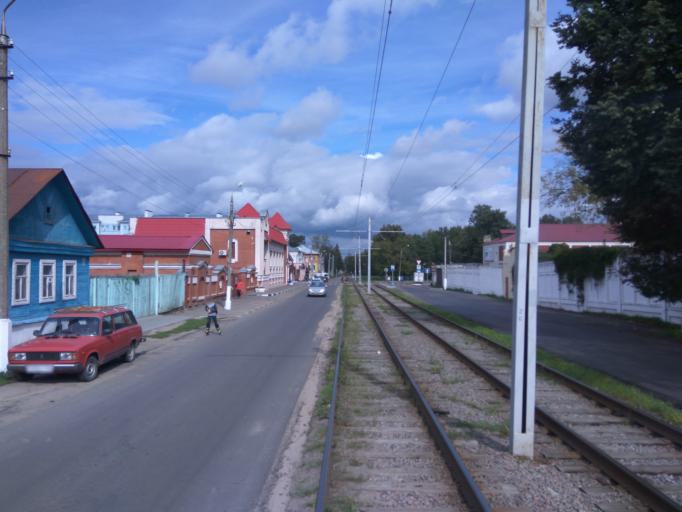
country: RU
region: Moskovskaya
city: Kolomna
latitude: 55.0980
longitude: 38.7743
